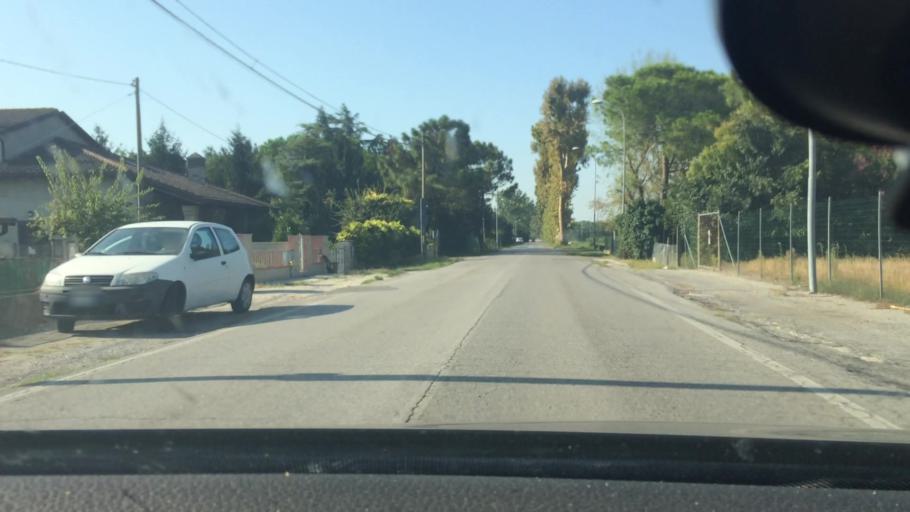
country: IT
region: Emilia-Romagna
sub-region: Provincia di Ferrara
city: Lagosanto
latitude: 44.7531
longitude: 12.1376
